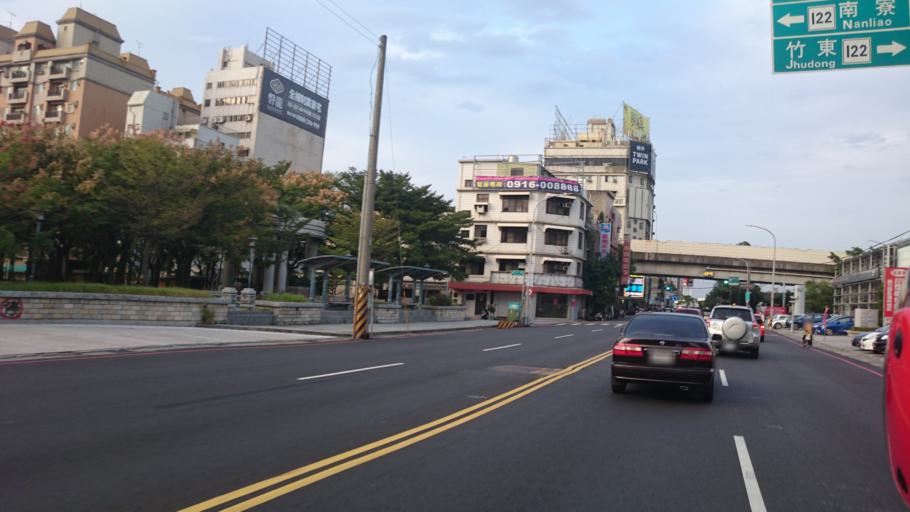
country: TW
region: Taiwan
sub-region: Hsinchu
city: Hsinchu
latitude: 24.8012
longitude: 120.9828
